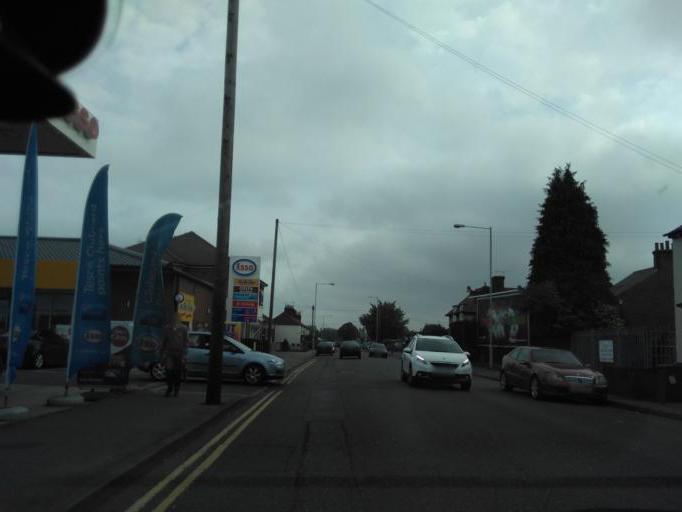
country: GB
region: England
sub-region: Kent
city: Canterbury
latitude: 51.2904
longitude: 1.1001
